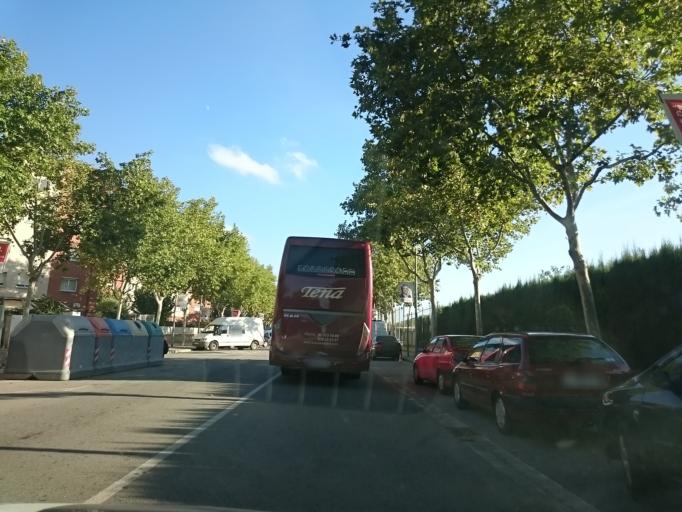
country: ES
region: Catalonia
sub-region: Provincia de Barcelona
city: Palleja
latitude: 41.4212
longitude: 2.0006
